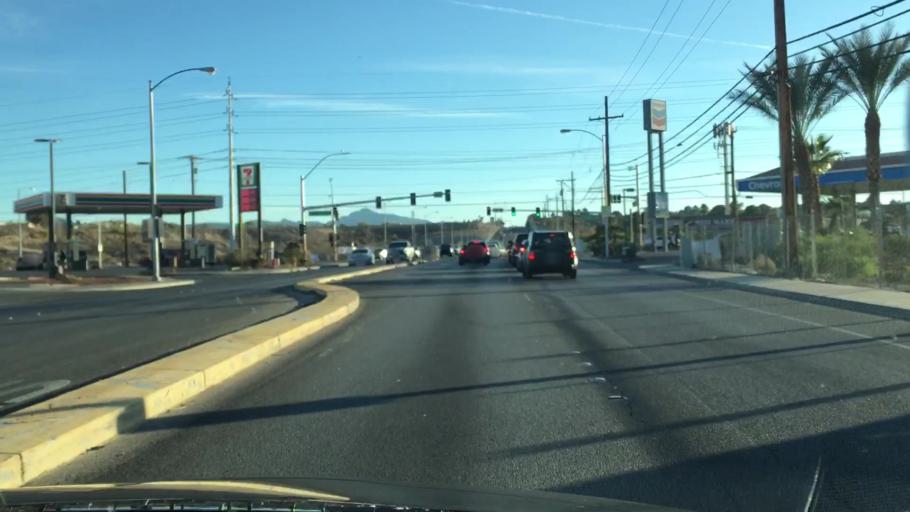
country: US
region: Nevada
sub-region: Clark County
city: Whitney
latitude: 36.0866
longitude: -115.0732
